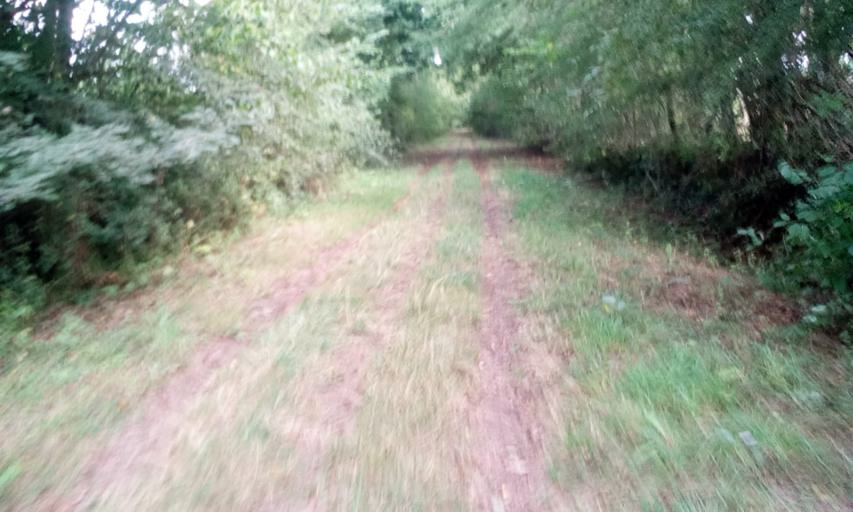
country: FR
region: Lower Normandy
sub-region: Departement du Calvados
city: Argences
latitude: 49.1264
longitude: -0.1375
